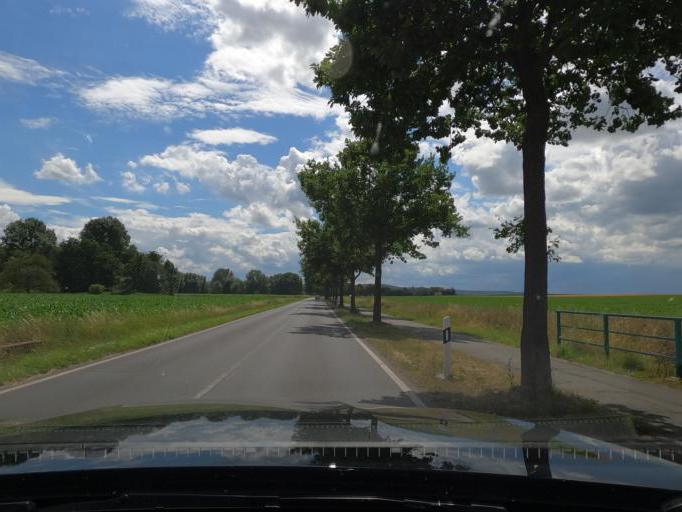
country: DE
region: Lower Saxony
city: Lengede
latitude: 52.1703
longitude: 10.3068
